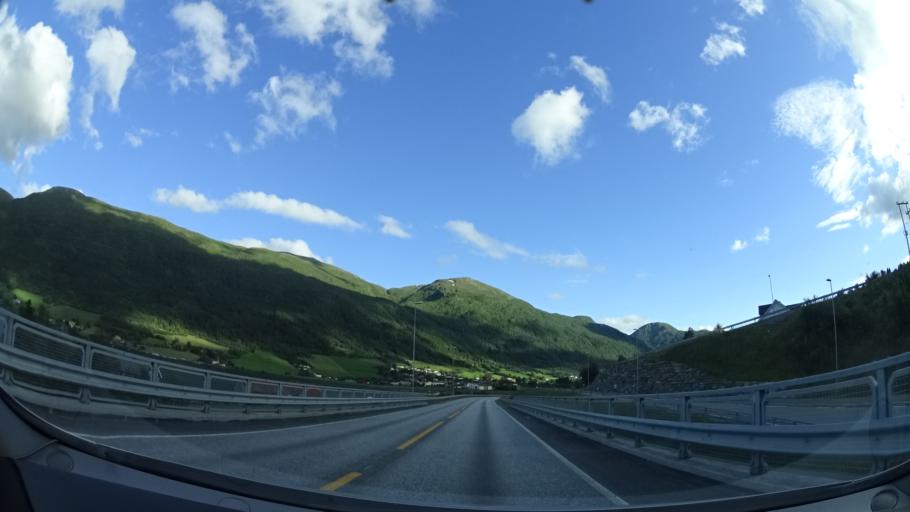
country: NO
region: More og Romsdal
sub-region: Gjemnes
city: Batnfjordsora
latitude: 62.9022
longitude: 7.6755
